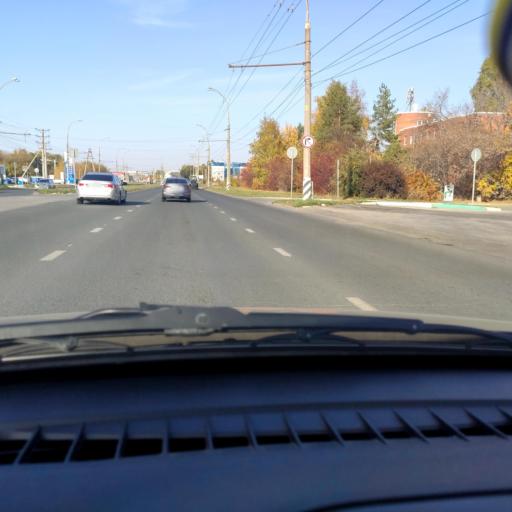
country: RU
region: Samara
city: Tol'yatti
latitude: 53.5489
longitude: 49.3024
